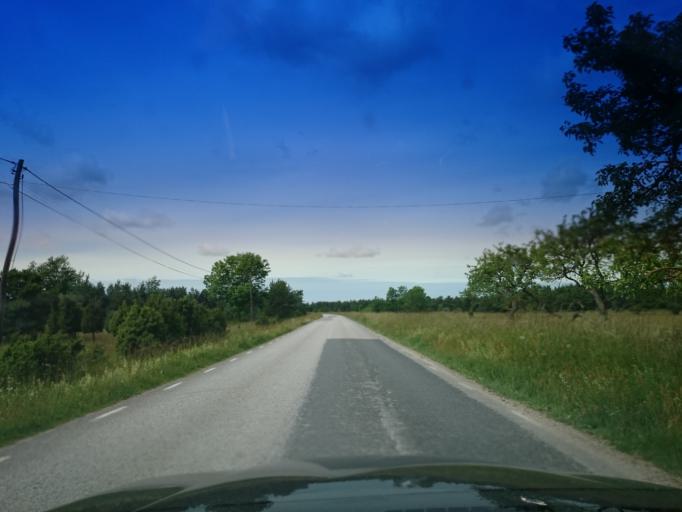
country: SE
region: Gotland
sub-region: Gotland
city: Hemse
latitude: 57.2536
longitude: 18.5945
